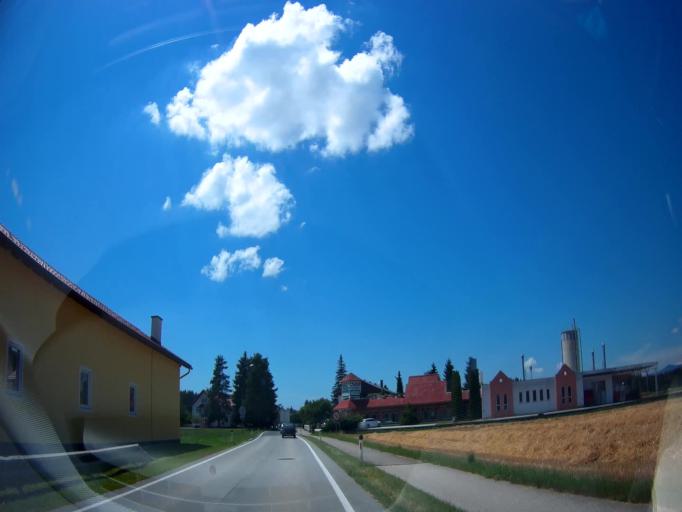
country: AT
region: Carinthia
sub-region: Politischer Bezirk Volkermarkt
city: Globasnitz
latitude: 46.6050
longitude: 14.7159
